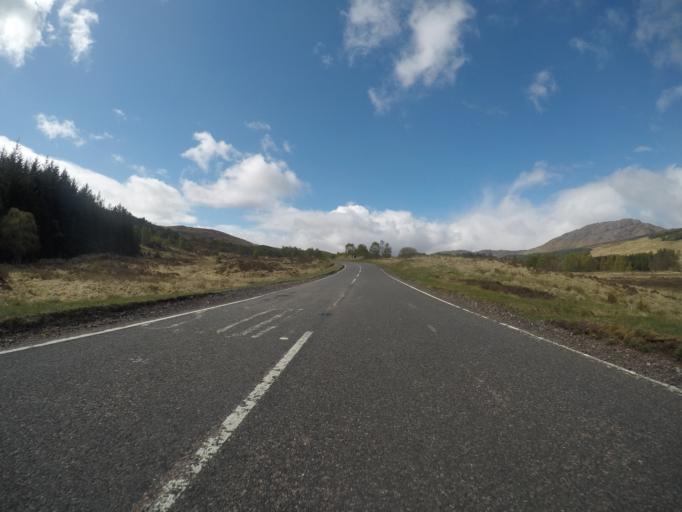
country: GB
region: Scotland
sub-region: Highland
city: Spean Bridge
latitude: 57.1282
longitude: -4.9634
